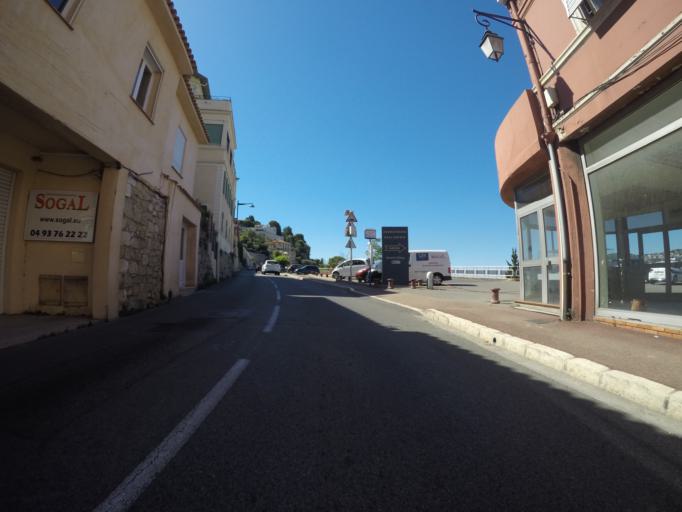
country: FR
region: Provence-Alpes-Cote d'Azur
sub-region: Departement des Alpes-Maritimes
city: Beaulieu-sur-Mer
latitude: 43.7011
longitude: 7.3264
